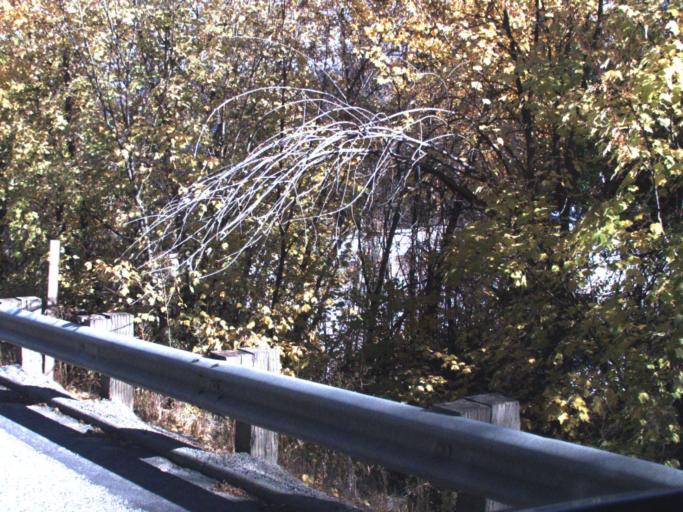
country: US
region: Washington
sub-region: Stevens County
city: Kettle Falls
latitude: 48.6263
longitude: -118.1249
